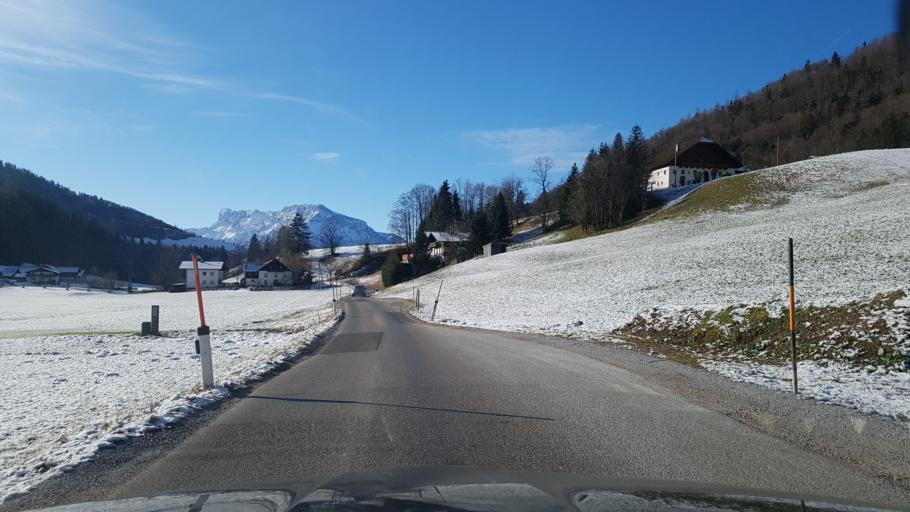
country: AT
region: Salzburg
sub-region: Politischer Bezirk Salzburg-Umgebung
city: Koppl
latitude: 47.7770
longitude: 13.1400
